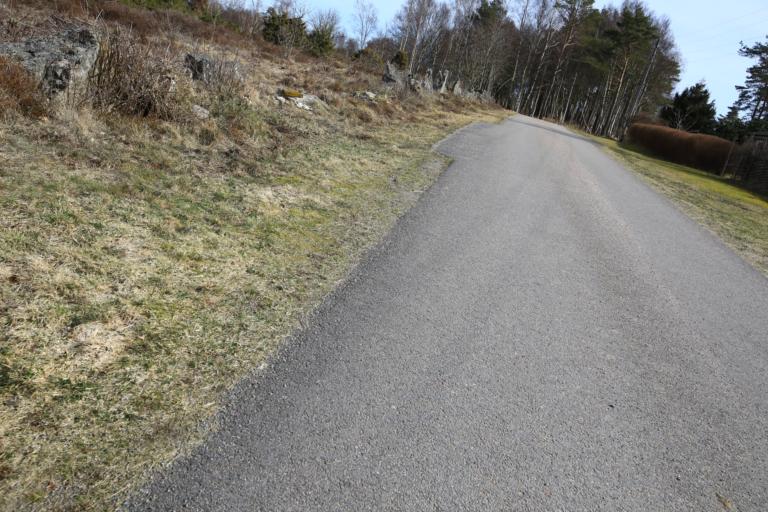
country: SE
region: Halland
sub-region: Kungsbacka Kommun
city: Frillesas
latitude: 57.2697
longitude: 12.1185
